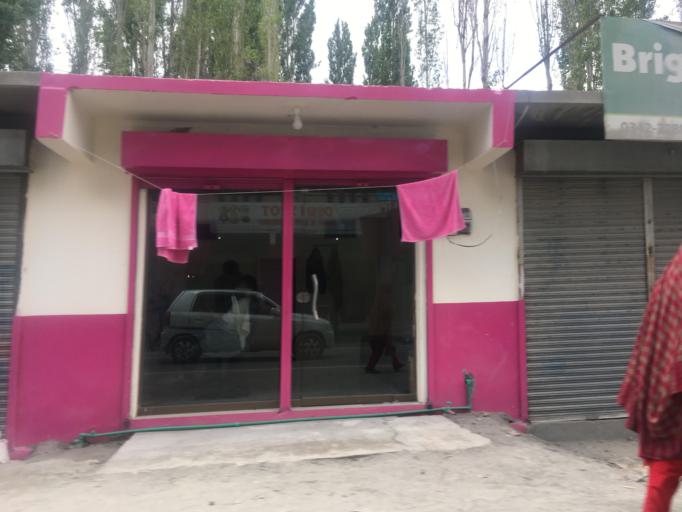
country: PK
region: Gilgit-Baltistan
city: Skardu
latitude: 35.2936
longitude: 75.6116
